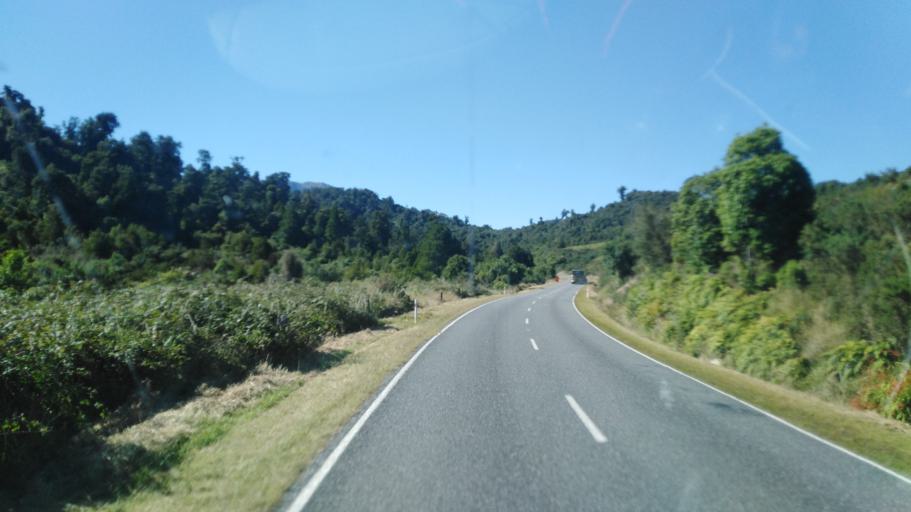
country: NZ
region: West Coast
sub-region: Buller District
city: Westport
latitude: -41.5311
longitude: 171.9900
